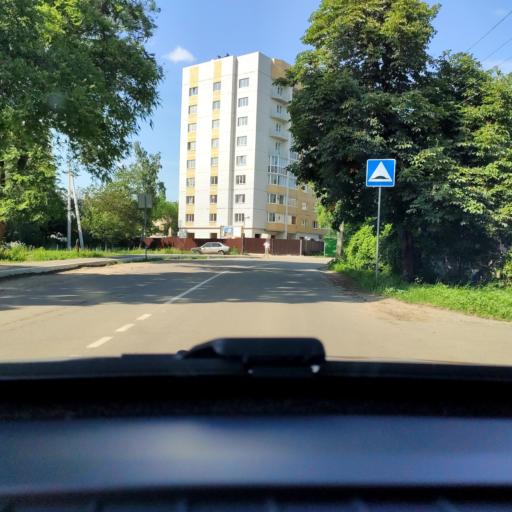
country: RU
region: Voronezj
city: Semiluki
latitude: 51.6920
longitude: 39.0128
